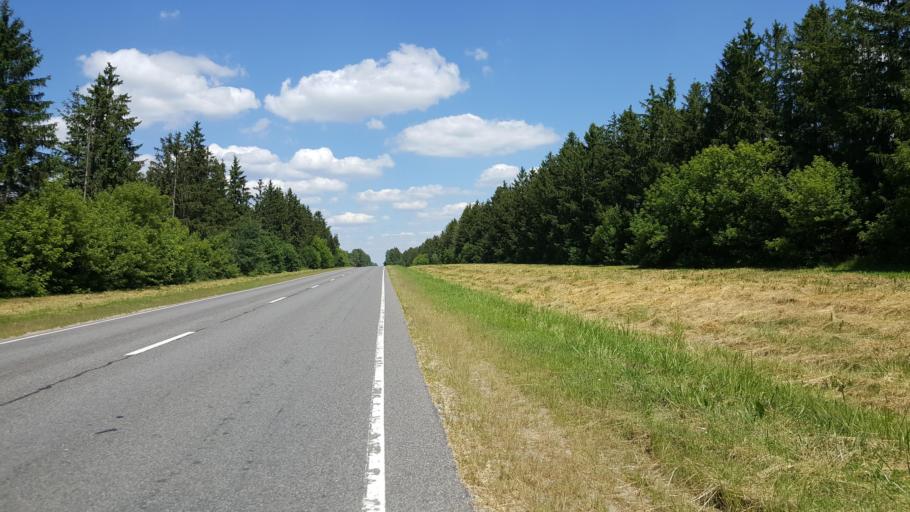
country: BY
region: Brest
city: Kamyanyets
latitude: 52.4198
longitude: 23.7877
